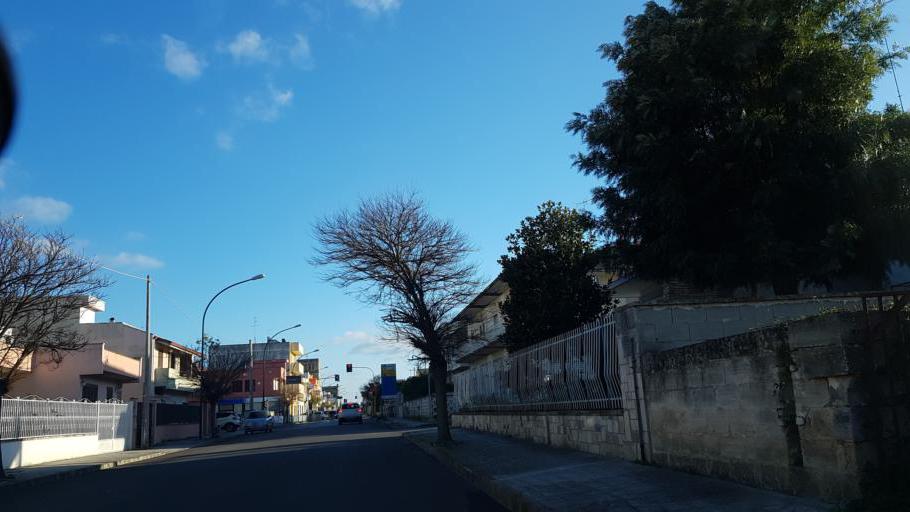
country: IT
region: Apulia
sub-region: Provincia di Lecce
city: Squinzano
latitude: 40.4422
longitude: 18.0350
